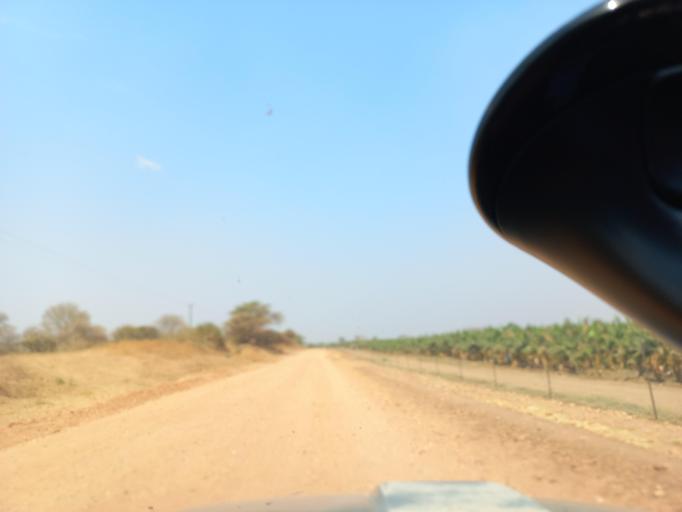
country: ZW
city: Chirundu
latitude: -15.9309
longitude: 28.9589
